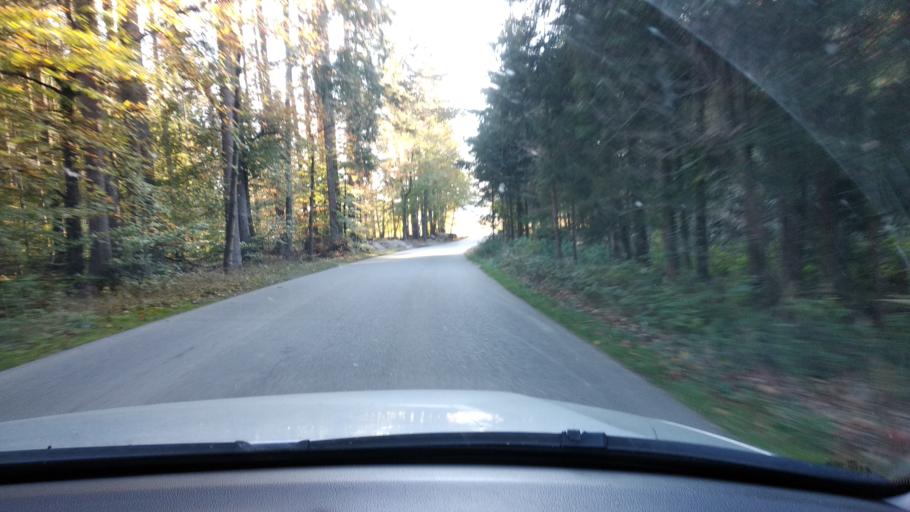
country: DE
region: Bavaria
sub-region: Upper Bavaria
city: Glonn
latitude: 47.9792
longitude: 11.8421
